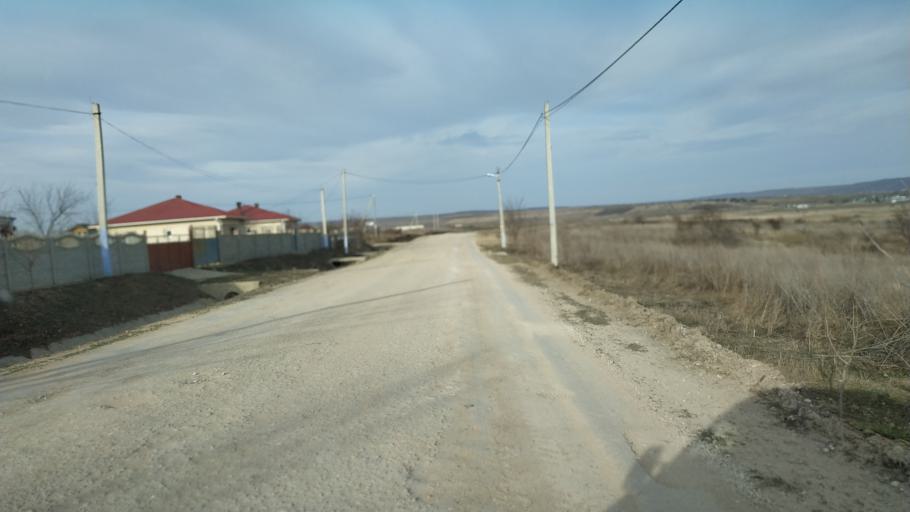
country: RO
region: Vaslui
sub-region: Comuna Dranceni
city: Dranceni
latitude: 46.8452
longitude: 28.1900
